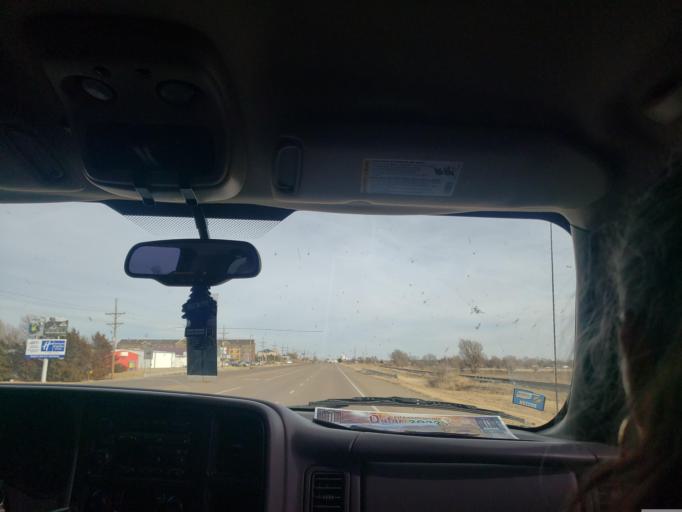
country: US
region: Kansas
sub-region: Ford County
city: Dodge City
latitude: 37.7549
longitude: -100.0611
